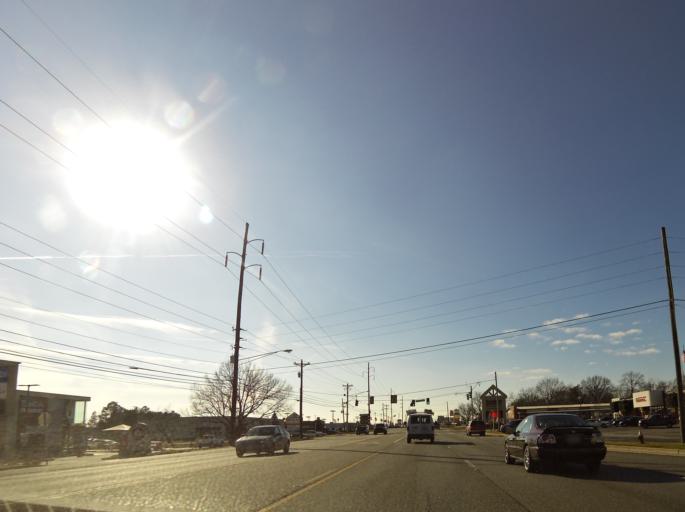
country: US
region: Georgia
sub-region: Houston County
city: Centerville
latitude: 32.6183
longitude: -83.6752
